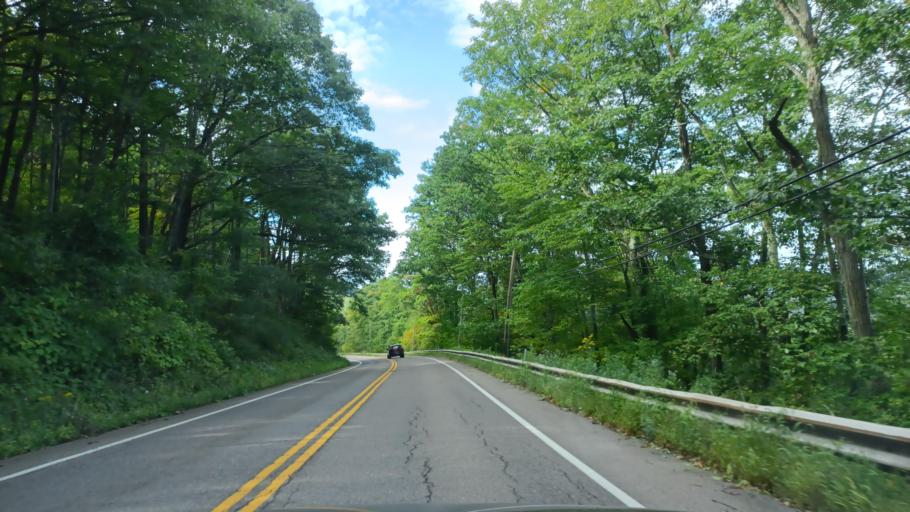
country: US
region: Maryland
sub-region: Garrett County
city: Mountain Lake Park
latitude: 39.3005
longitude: -79.4196
